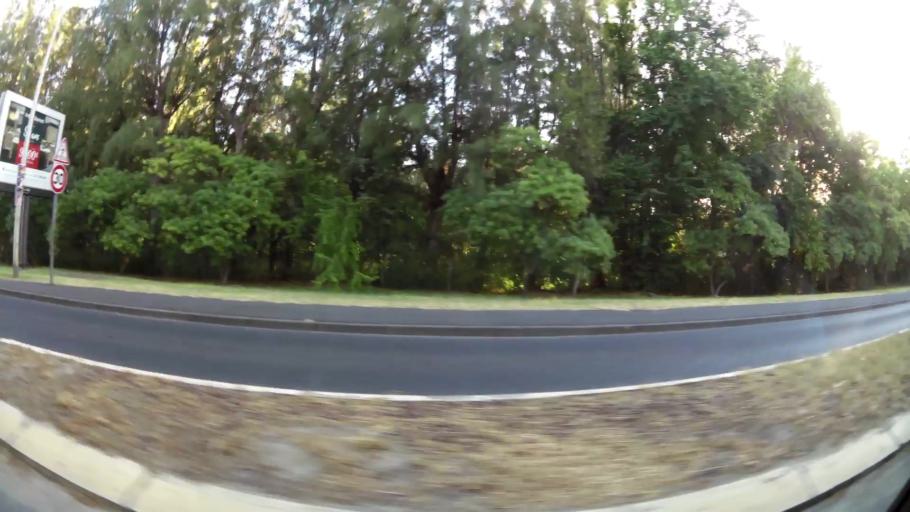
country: RE
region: Reunion
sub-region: Reunion
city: Trois-Bassins
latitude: -21.0915
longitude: 55.2354
